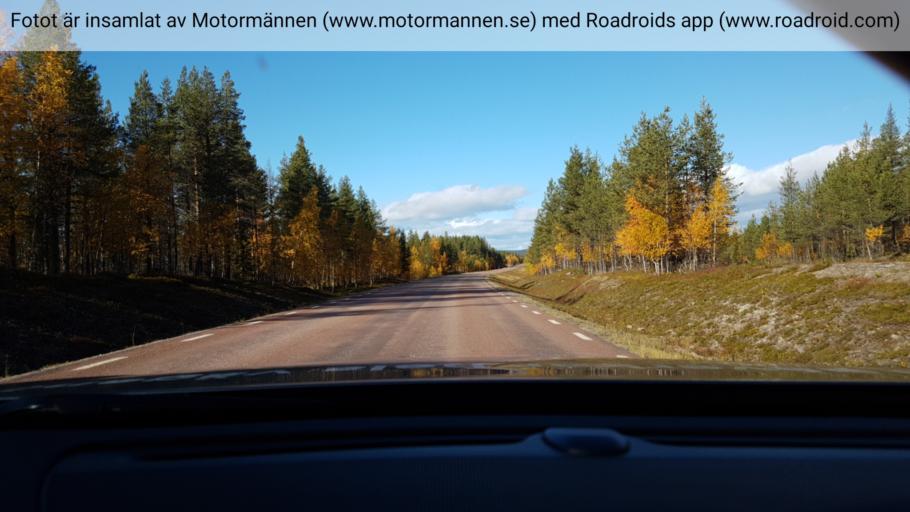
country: SE
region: Norrbotten
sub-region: Arjeplogs Kommun
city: Arjeplog
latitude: 66.0036
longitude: 18.1164
